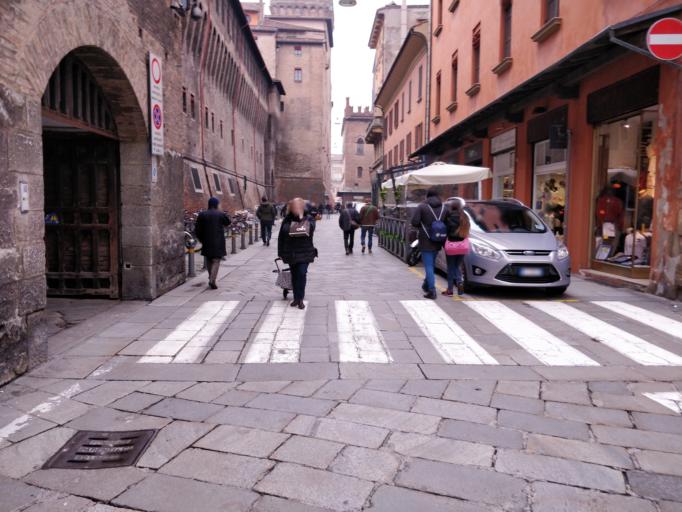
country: IT
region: Emilia-Romagna
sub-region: Provincia di Bologna
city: Bologna
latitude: 44.4939
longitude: 11.3410
